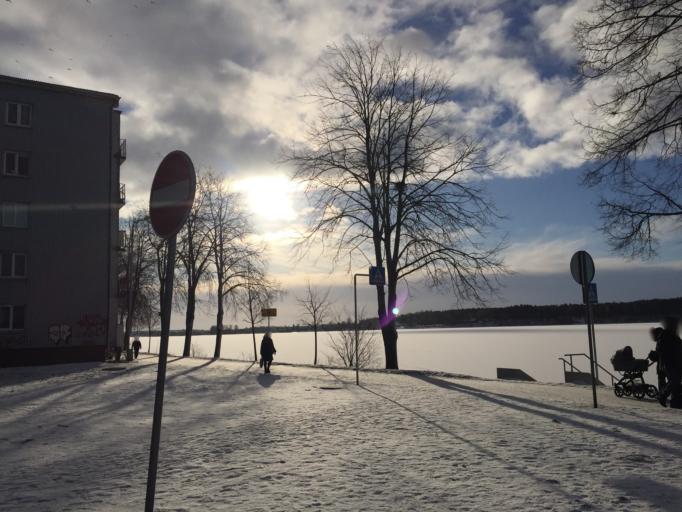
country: LV
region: Kekava
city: Balozi
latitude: 56.9106
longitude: 24.1745
